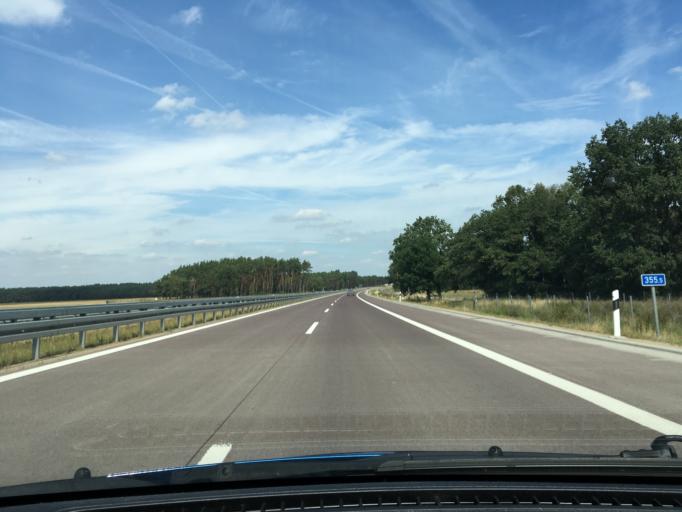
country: DE
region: Mecklenburg-Vorpommern
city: Ludwigslust
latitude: 53.3590
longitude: 11.5155
